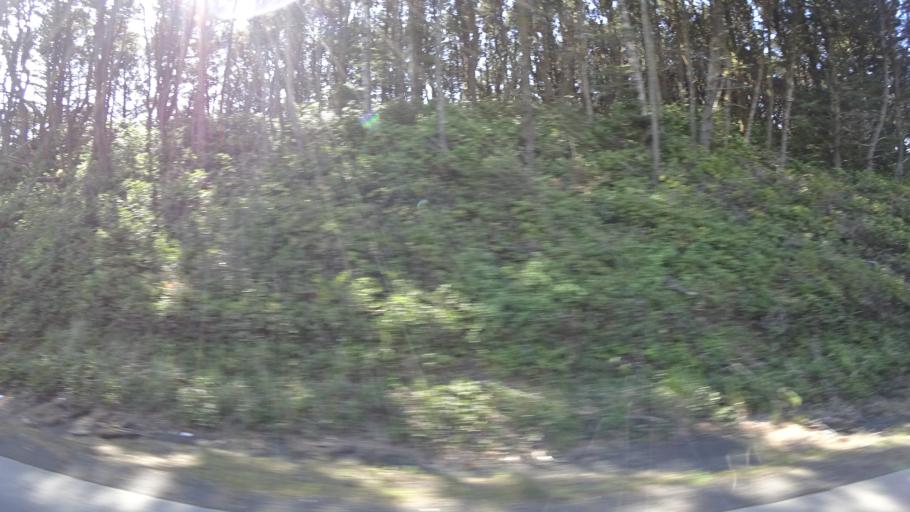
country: US
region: Oregon
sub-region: Lincoln County
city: Newport
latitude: 44.7136
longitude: -124.0584
